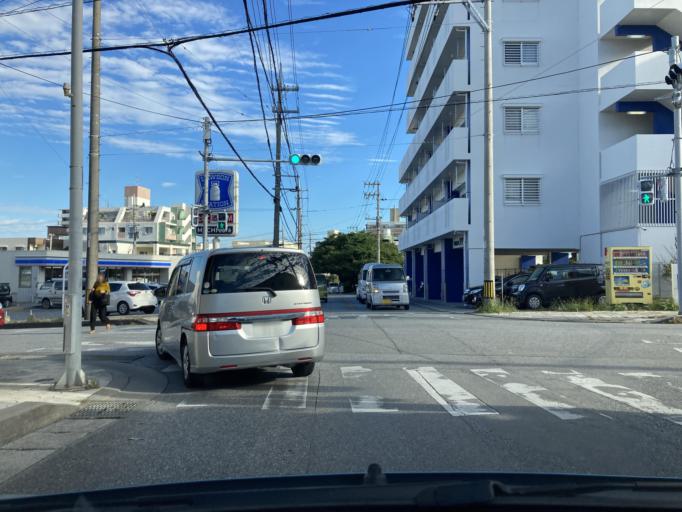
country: JP
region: Okinawa
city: Ginowan
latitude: 26.2731
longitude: 127.7411
